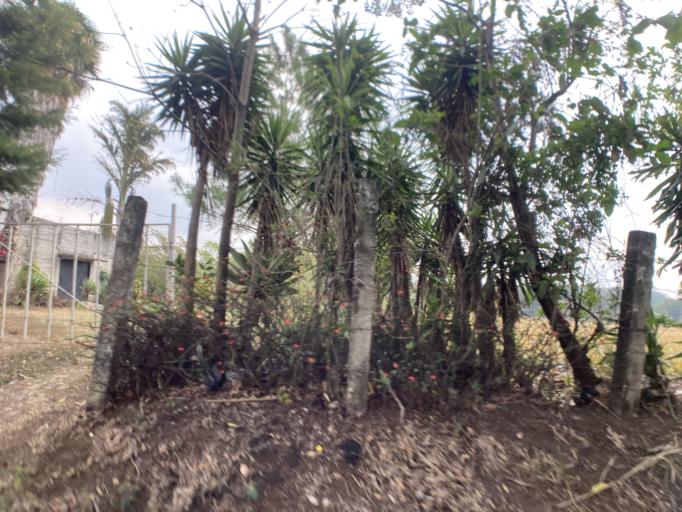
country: GT
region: Guatemala
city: Fraijanes
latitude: 14.3965
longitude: -90.4809
